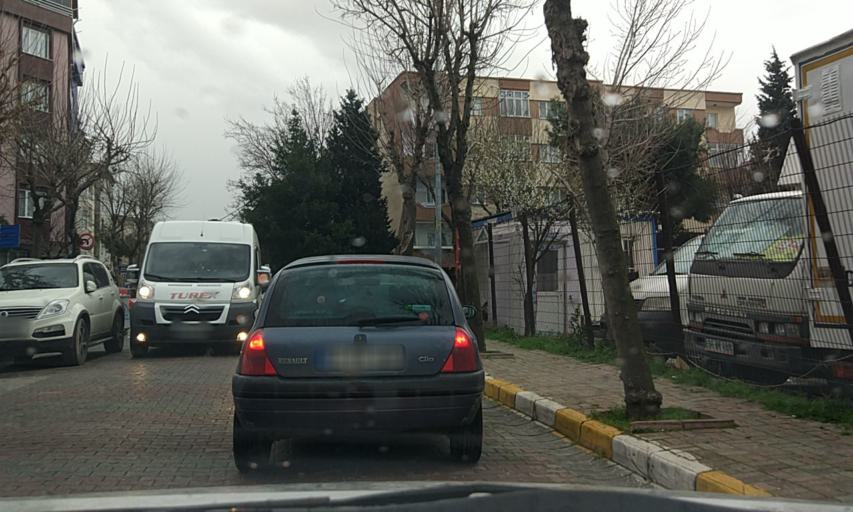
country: TR
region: Istanbul
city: Bagcilar
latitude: 41.0214
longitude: 28.8320
